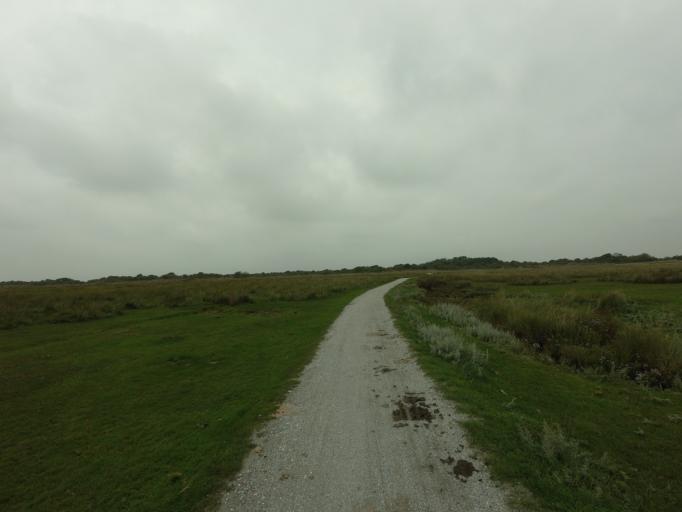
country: NL
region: Friesland
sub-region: Gemeente Schiermonnikoog
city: Schiermonnikoog
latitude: 53.4851
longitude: 6.2172
